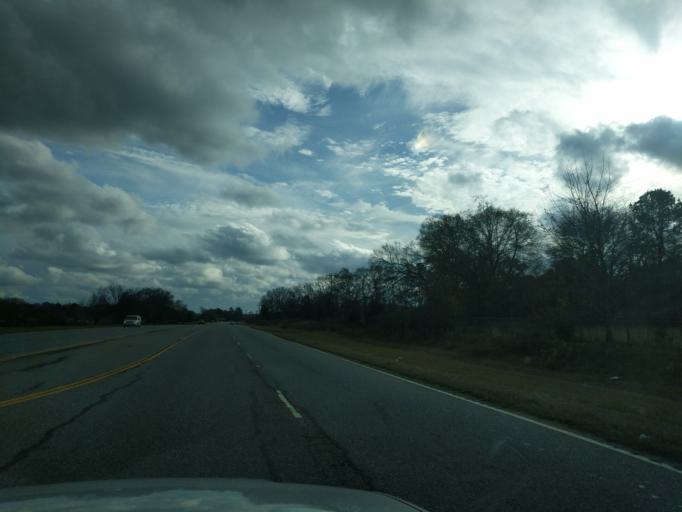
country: US
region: South Carolina
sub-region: Greenwood County
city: Ware Shoals
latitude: 34.4566
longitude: -82.2518
